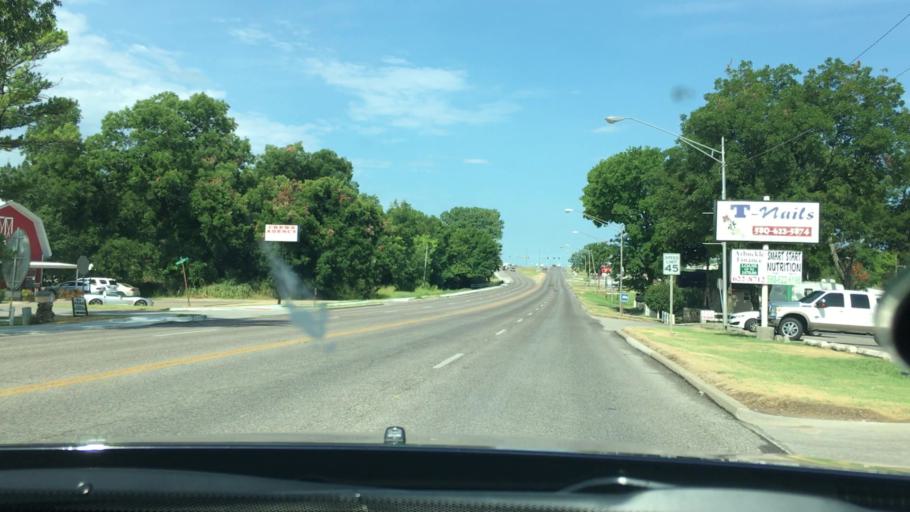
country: US
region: Oklahoma
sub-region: Murray County
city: Sulphur
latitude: 34.5064
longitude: -96.9970
